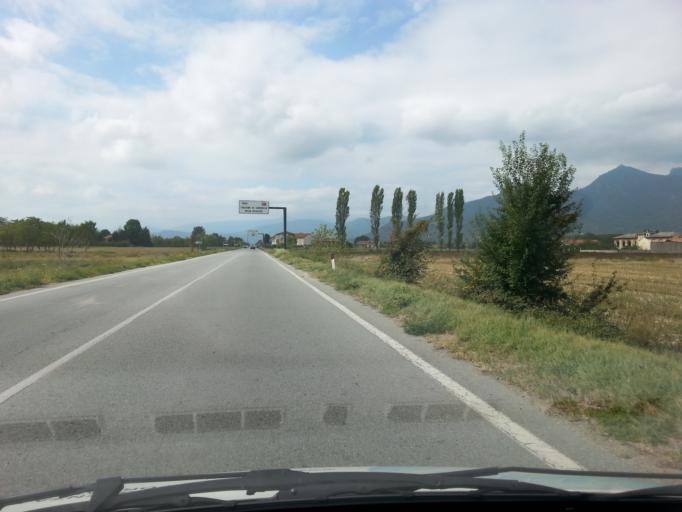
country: IT
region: Piedmont
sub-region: Provincia di Torino
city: Piossasco
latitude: 44.9653
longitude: 7.4249
